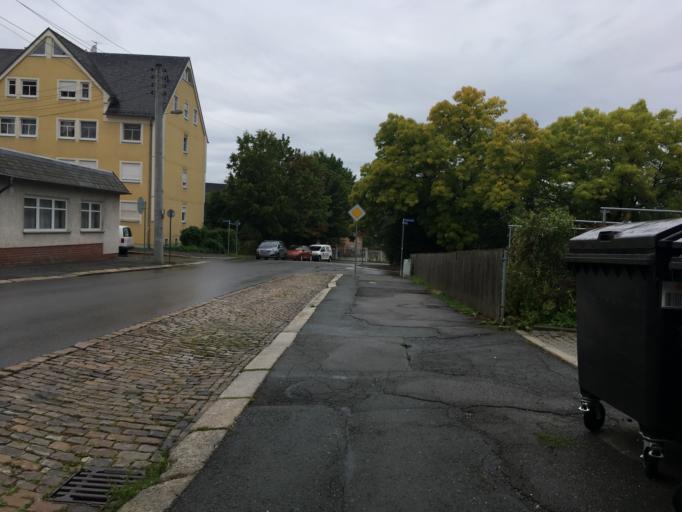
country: DE
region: Saxony
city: Glauchau
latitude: 50.8214
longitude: 12.5486
